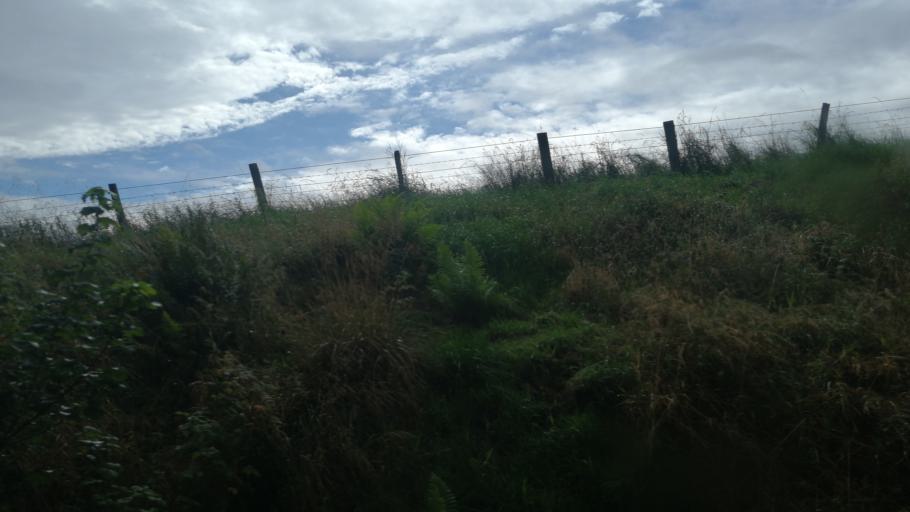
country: GB
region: Scotland
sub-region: Aberdeenshire
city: Huntly
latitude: 57.3527
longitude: -2.7613
